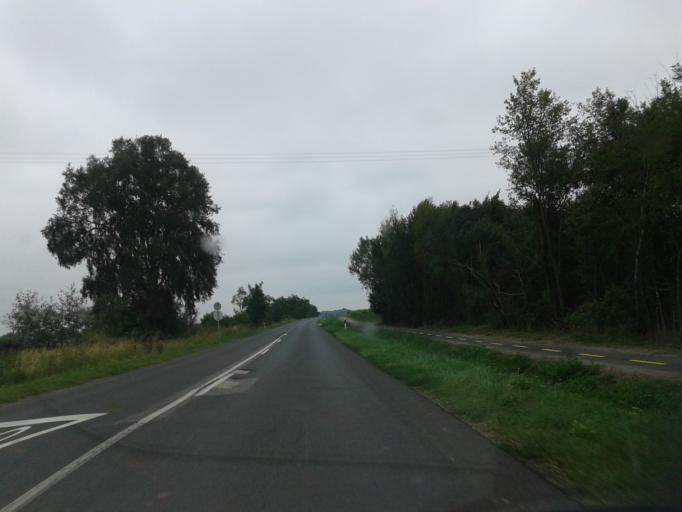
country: HU
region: Bacs-Kiskun
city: Akaszto
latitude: 46.6693
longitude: 19.2271
